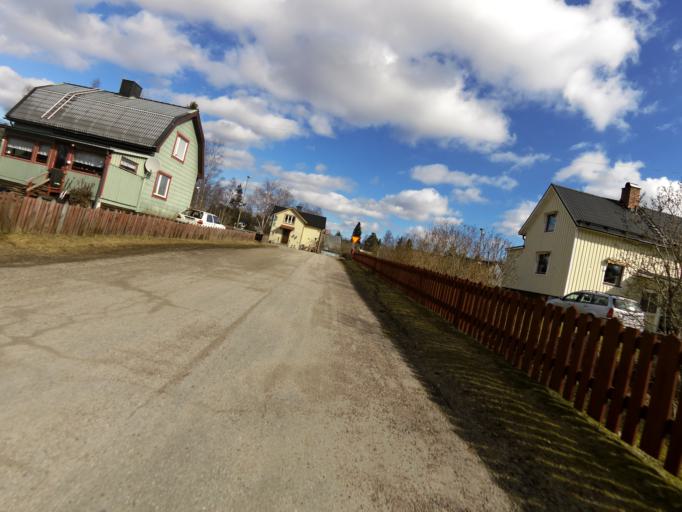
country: SE
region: Gaevleborg
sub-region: Hofors Kommun
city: Hofors
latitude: 60.5371
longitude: 16.2955
